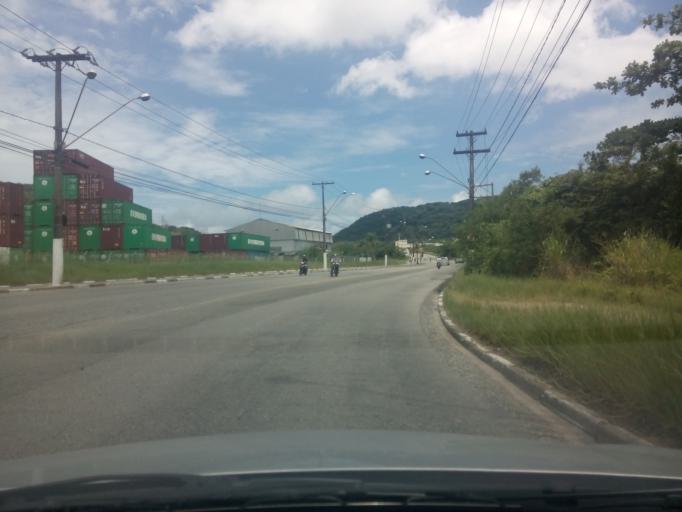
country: BR
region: Sao Paulo
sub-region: Guaruja
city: Guaruja
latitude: -23.9795
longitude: -46.2701
